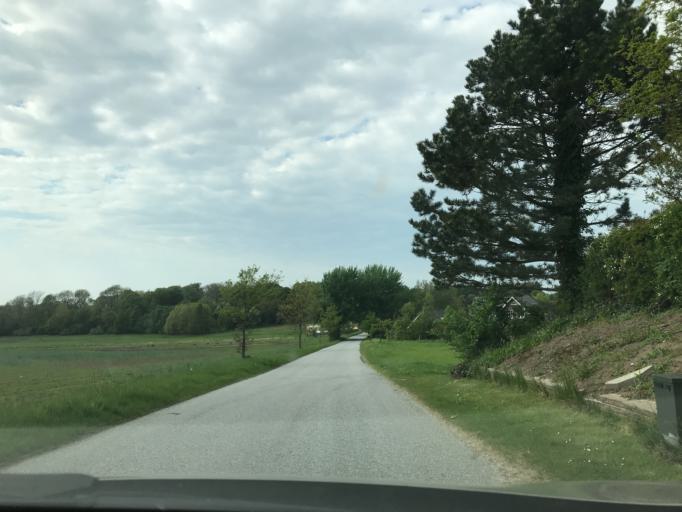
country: DK
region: South Denmark
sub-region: Assens Kommune
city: Assens
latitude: 55.3405
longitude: 9.9078
